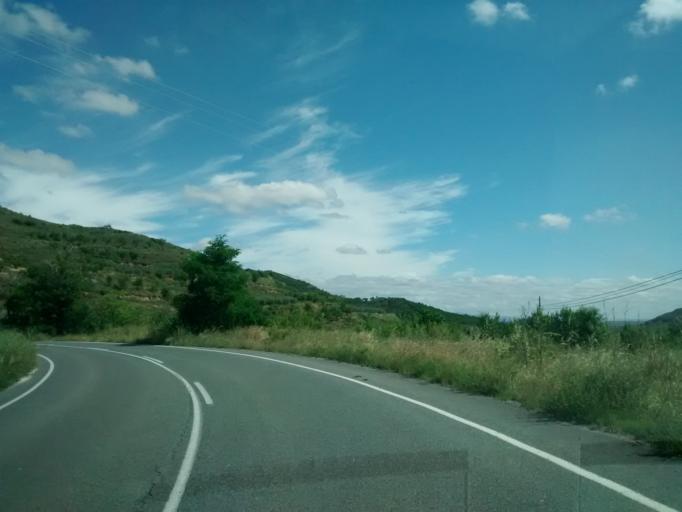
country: ES
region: La Rioja
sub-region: Provincia de La Rioja
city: Leza de Rio Leza
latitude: 42.3379
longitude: -2.4066
